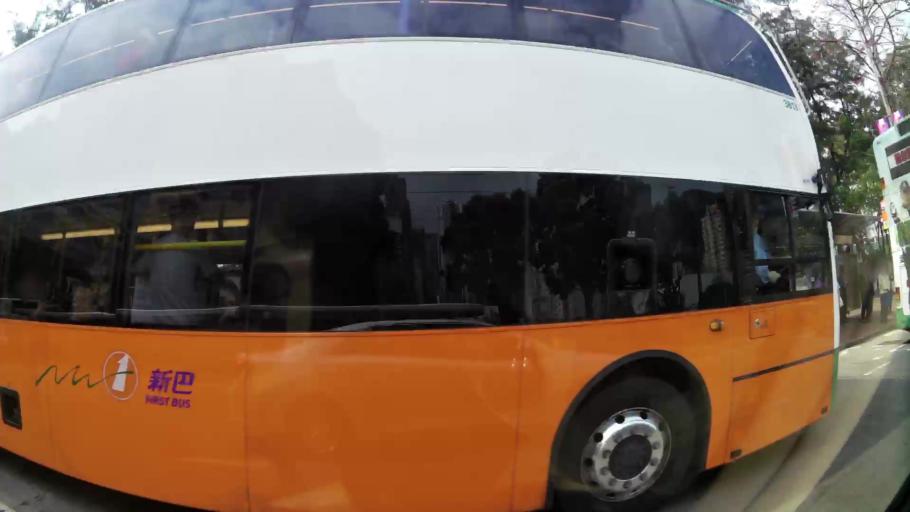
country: HK
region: Wanchai
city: Wan Chai
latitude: 22.2810
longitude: 114.1898
